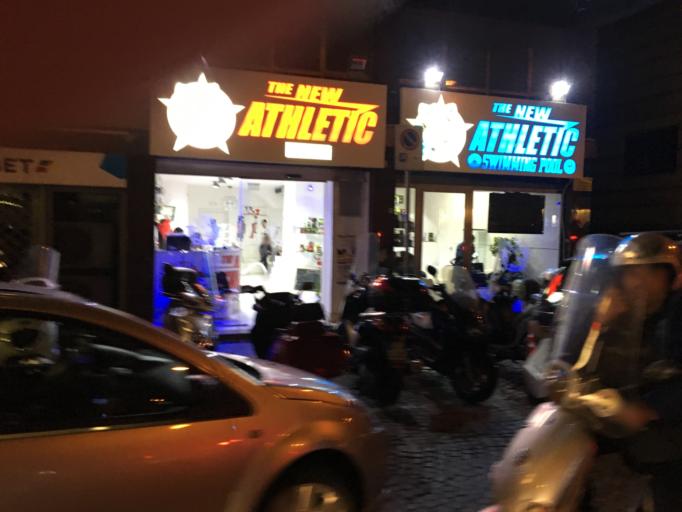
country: IT
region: Campania
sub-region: Provincia di Napoli
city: Napoli
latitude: 40.8406
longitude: 14.2541
